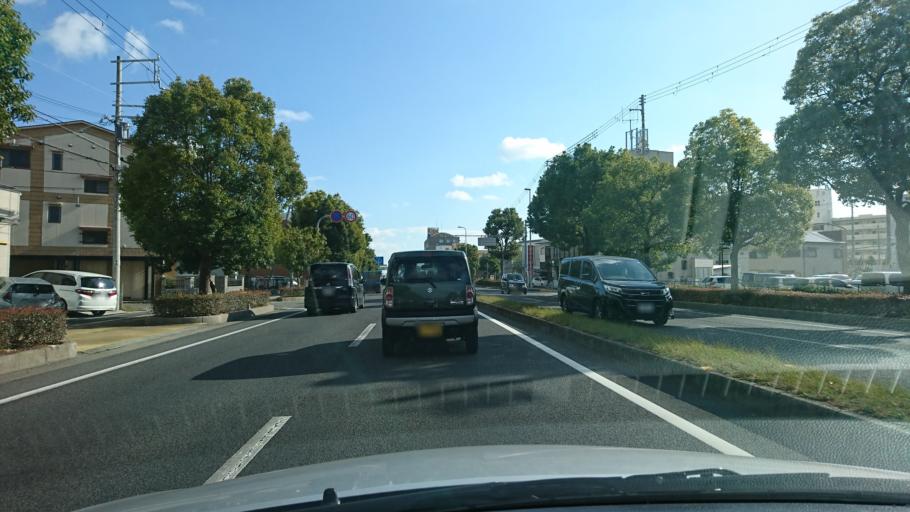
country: JP
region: Hyogo
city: Kakogawacho-honmachi
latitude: 34.7035
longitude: 134.8883
